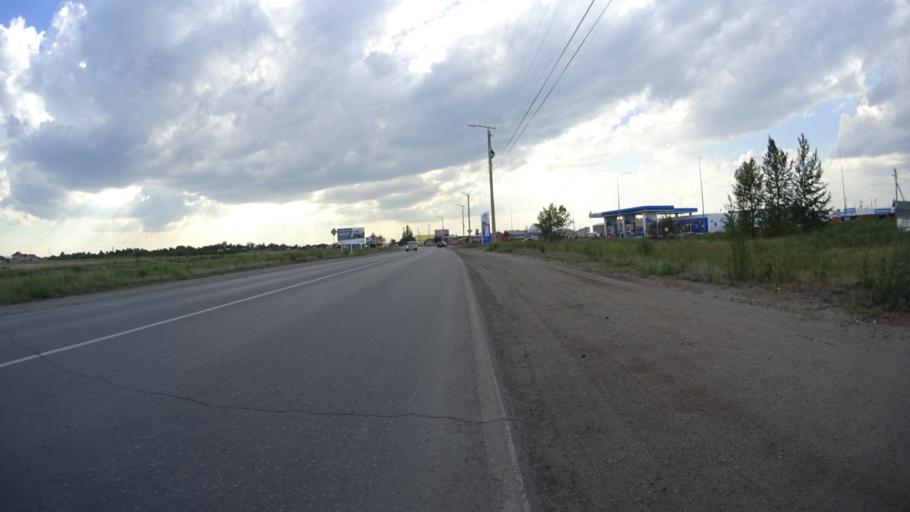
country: RU
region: Chelyabinsk
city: Troitsk
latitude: 54.0819
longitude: 61.5201
